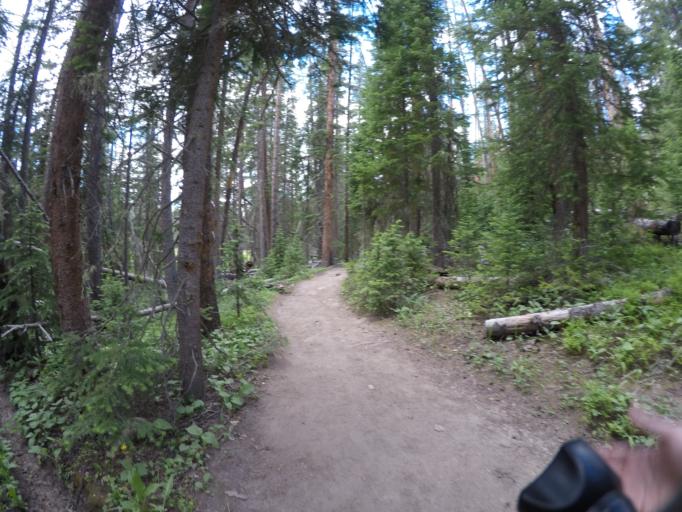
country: US
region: Colorado
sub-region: Grand County
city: Granby
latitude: 40.3091
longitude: -105.8206
